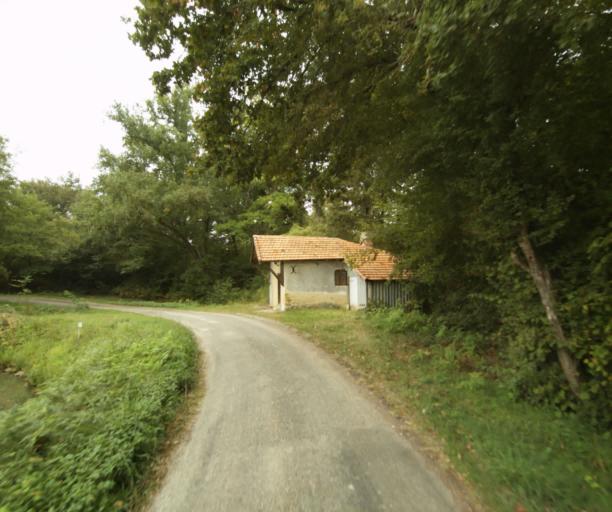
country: FR
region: Midi-Pyrenees
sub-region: Departement du Gers
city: Cazaubon
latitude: 43.9271
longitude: -0.1782
